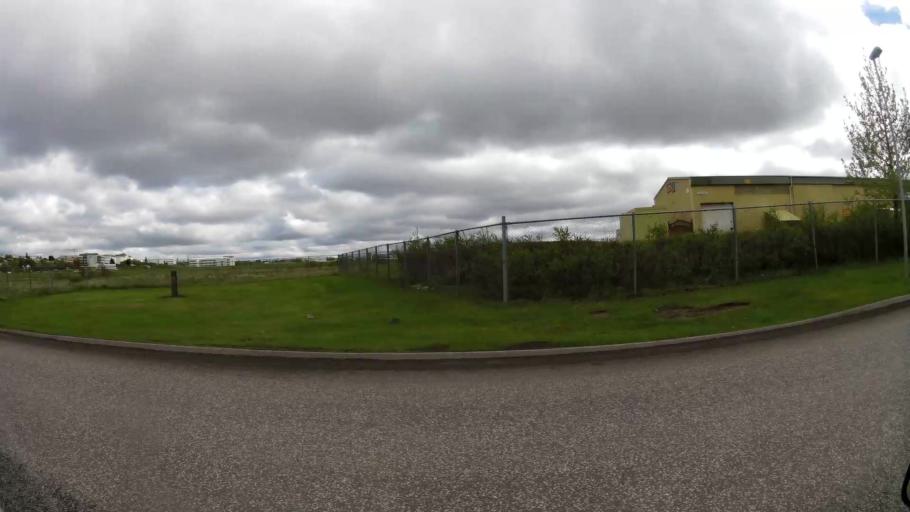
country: IS
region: Capital Region
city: Kopavogur
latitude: 64.1359
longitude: -21.9431
